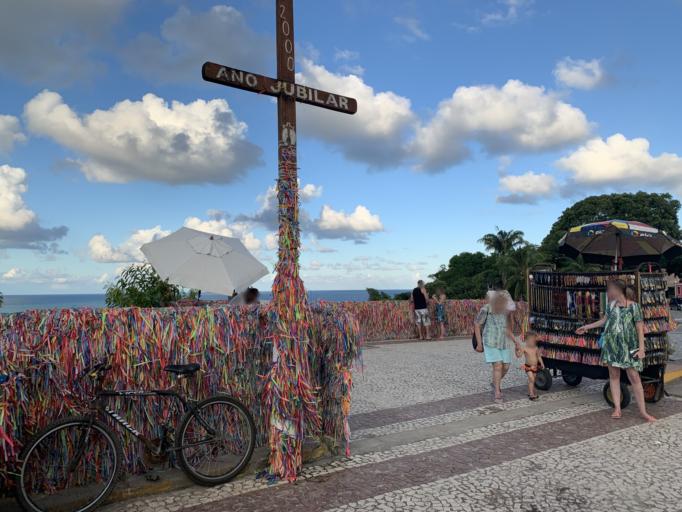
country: BR
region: Bahia
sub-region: Porto Seguro
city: Porto Seguro
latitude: -16.4892
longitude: -39.0727
